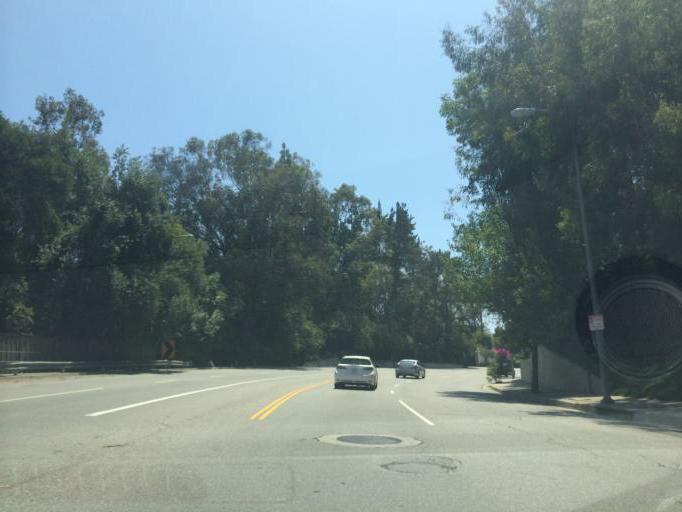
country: US
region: California
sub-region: Los Angeles County
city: Westwood, Los Angeles
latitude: 34.0800
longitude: -118.4282
